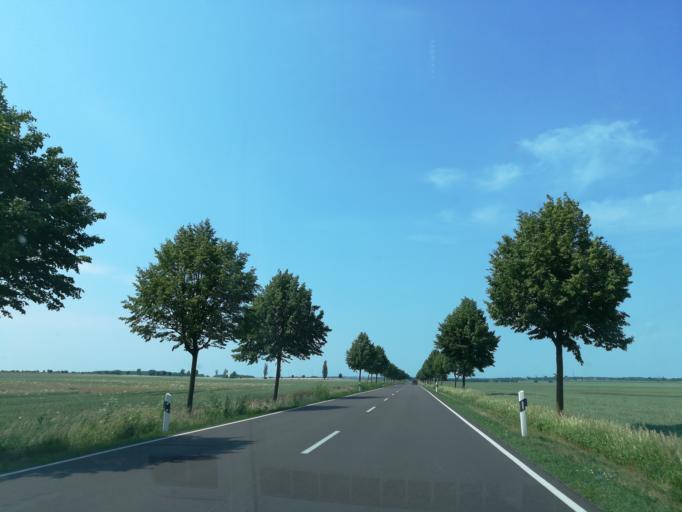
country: DE
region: Saxony-Anhalt
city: Schneidlingen
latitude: 51.9045
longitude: 11.4358
